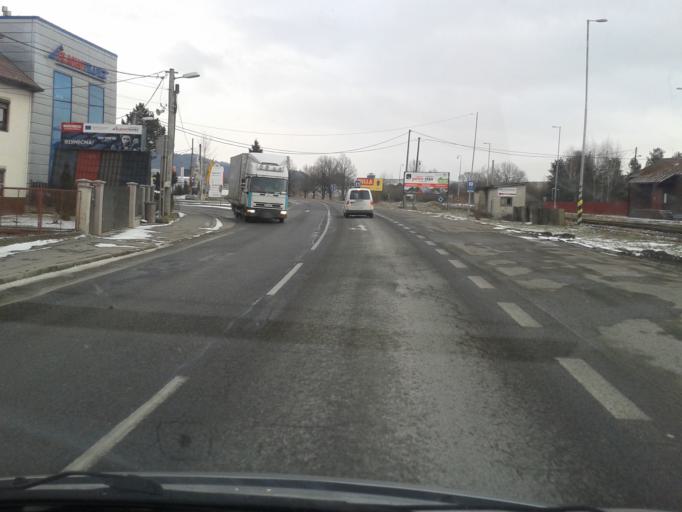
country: SK
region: Zilinsky
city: Tvrdosin
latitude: 49.3386
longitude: 19.5652
